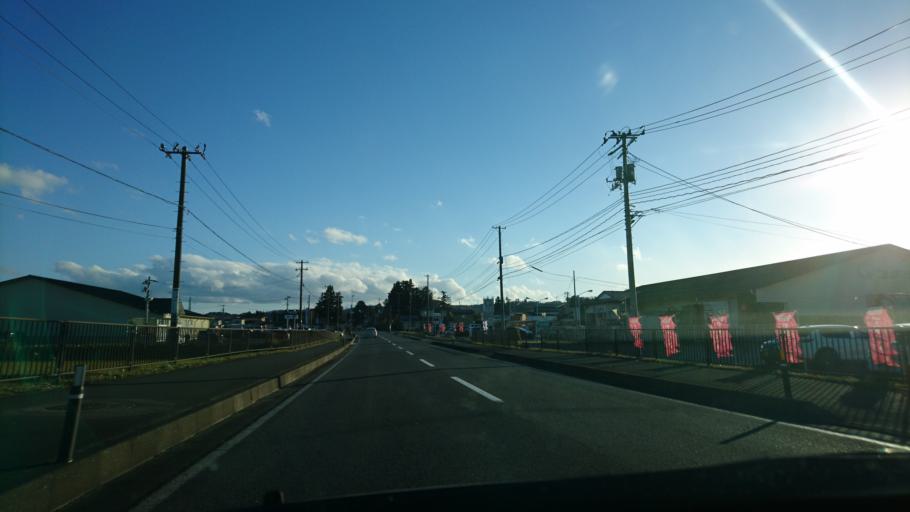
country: JP
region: Iwate
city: Ichinoseki
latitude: 38.9818
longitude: 141.1164
